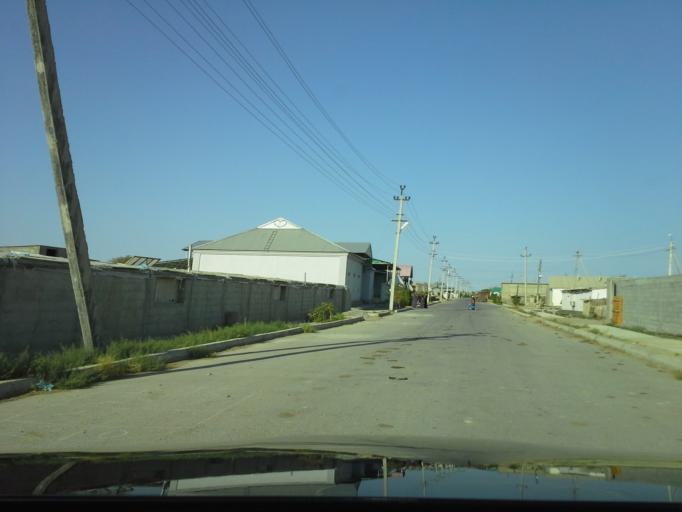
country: TM
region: Ahal
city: Abadan
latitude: 38.1719
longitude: 58.1015
